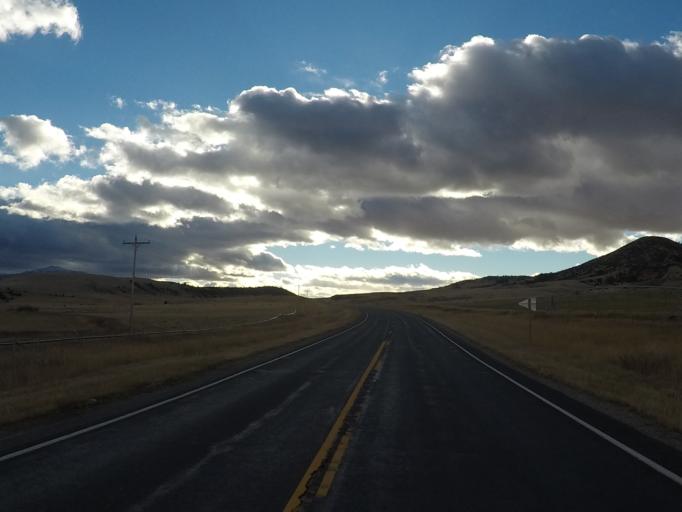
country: US
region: Montana
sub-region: Jefferson County
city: Whitehall
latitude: 45.9163
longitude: -111.9319
